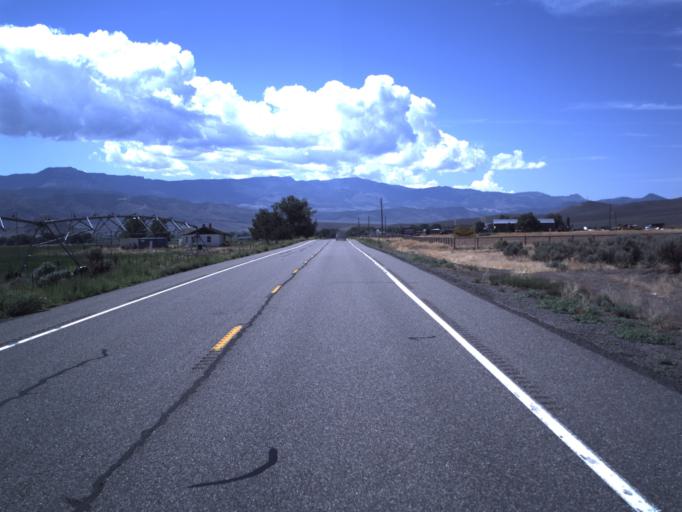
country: US
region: Utah
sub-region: Piute County
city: Junction
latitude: 38.2571
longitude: -112.2206
